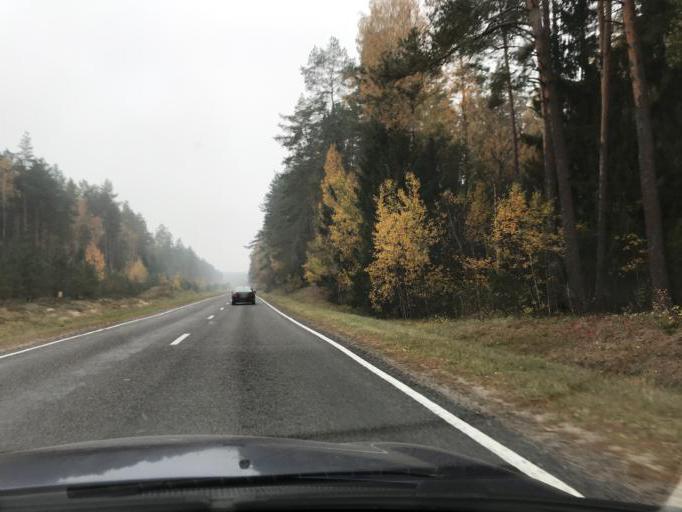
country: LT
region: Alytaus apskritis
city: Druskininkai
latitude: 53.8785
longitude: 23.9014
